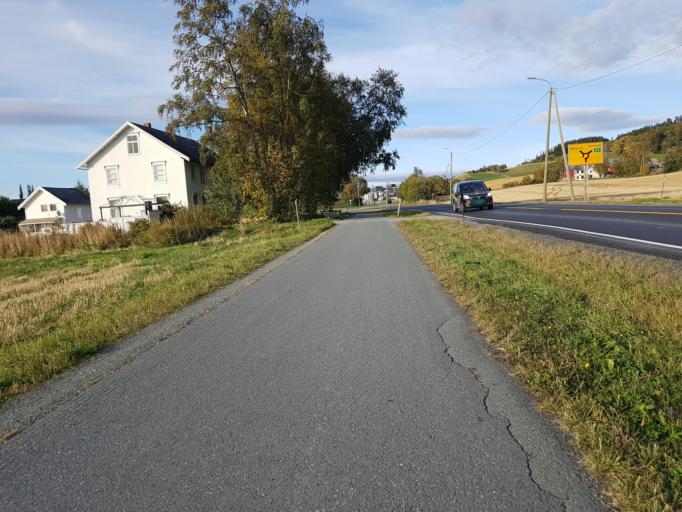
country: NO
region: Sor-Trondelag
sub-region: Trondheim
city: Trondheim
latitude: 63.3812
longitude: 10.4351
